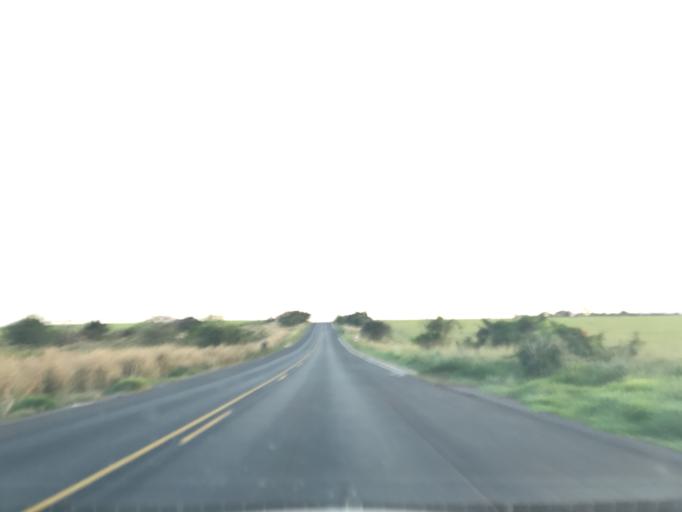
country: BR
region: Sao Paulo
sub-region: Pirapozinho
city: Pirapozinho
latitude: -22.4077
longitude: -51.6277
